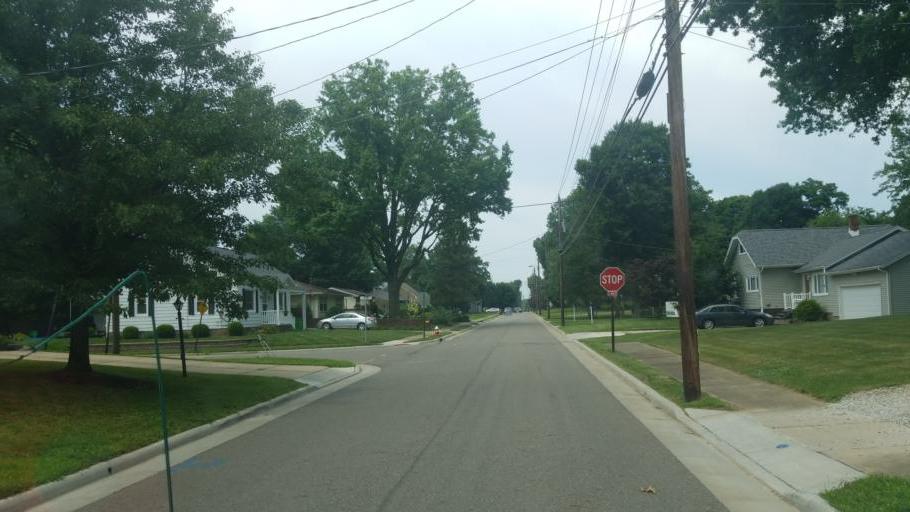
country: US
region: Ohio
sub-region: Stark County
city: North Canton
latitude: 40.8799
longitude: -81.3928
